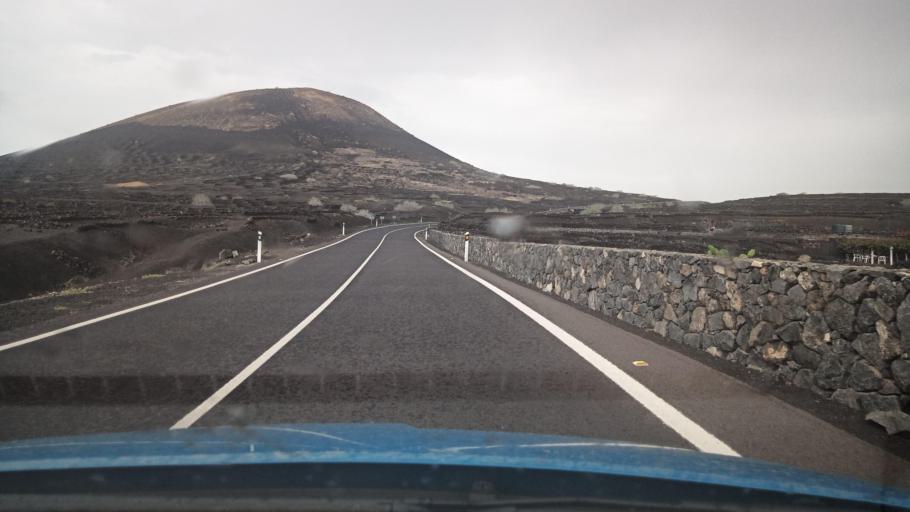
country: ES
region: Canary Islands
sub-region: Provincia de Las Palmas
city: Yaiza
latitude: 28.9612
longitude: -13.7281
